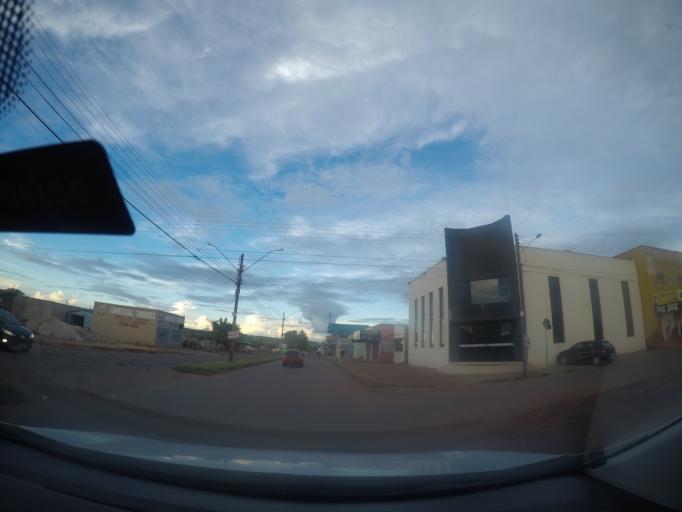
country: BR
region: Goias
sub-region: Goianira
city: Goianira
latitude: -16.5752
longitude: -49.3846
